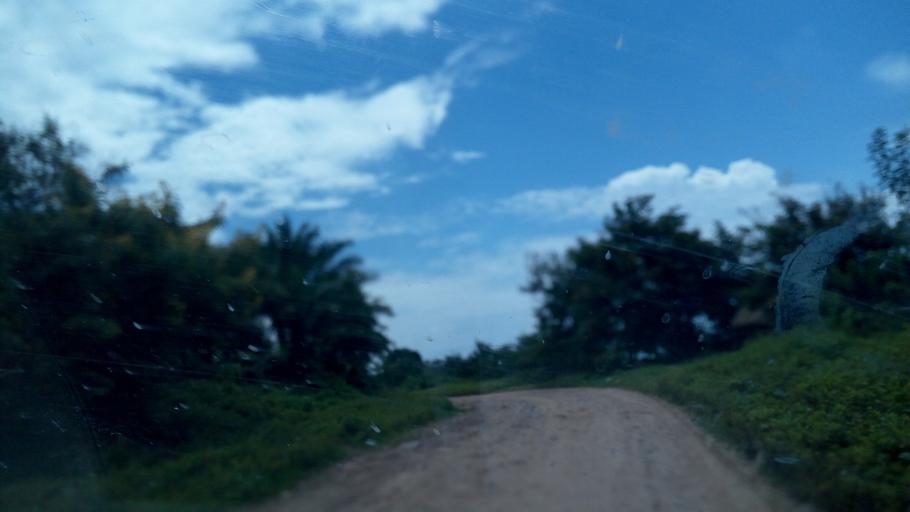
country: CD
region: South Kivu
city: Uvira
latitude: -3.5964
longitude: 29.1456
